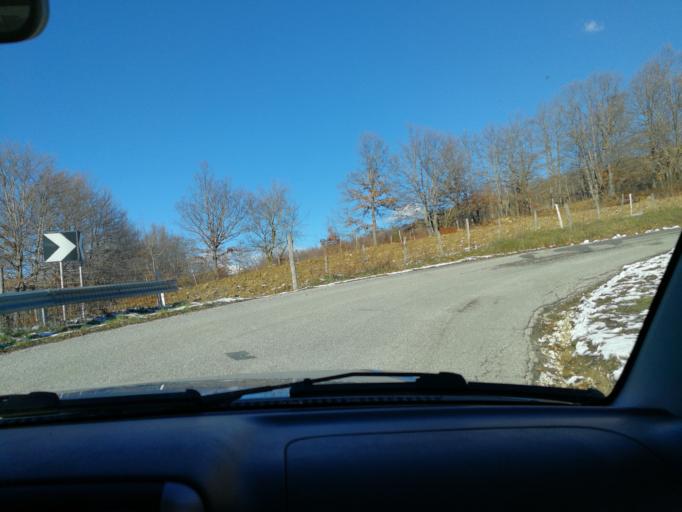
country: IT
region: Latium
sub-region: Provincia di Rieti
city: Accumoli
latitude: 42.6696
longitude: 13.2783
